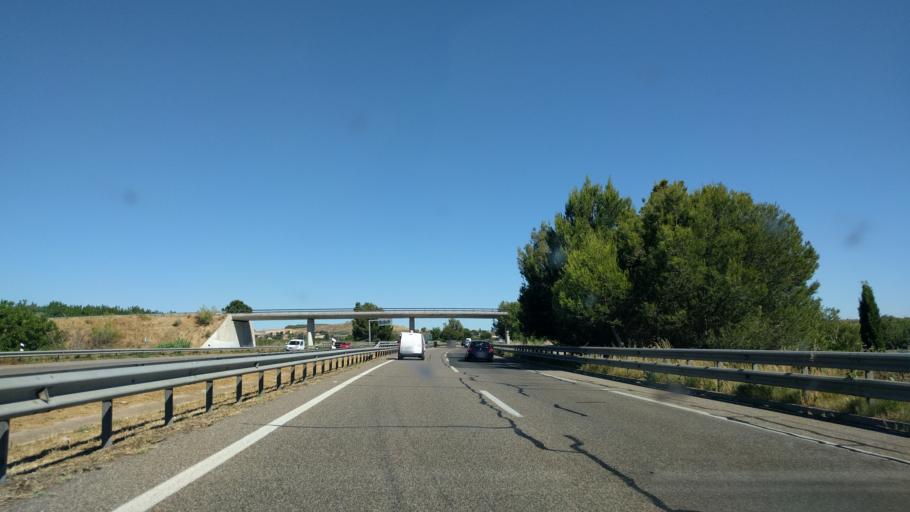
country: ES
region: Catalonia
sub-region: Provincia de Lleida
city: Alcoletge
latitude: 41.6540
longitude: 0.6661
